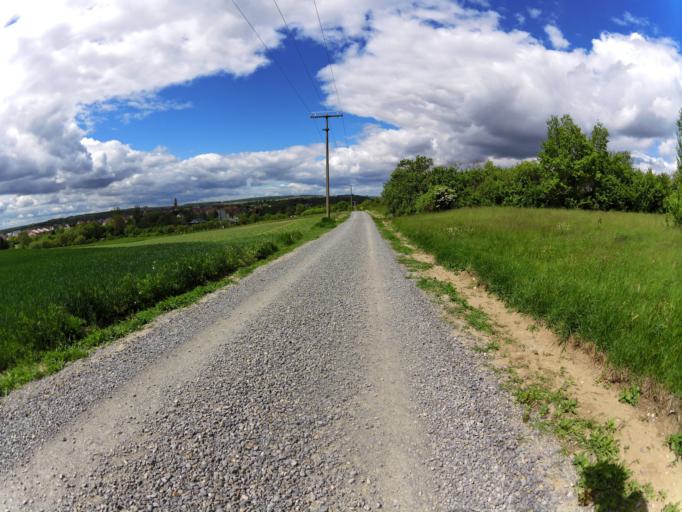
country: DE
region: Bavaria
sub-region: Regierungsbezirk Unterfranken
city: Volkach
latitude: 49.8704
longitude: 10.2378
